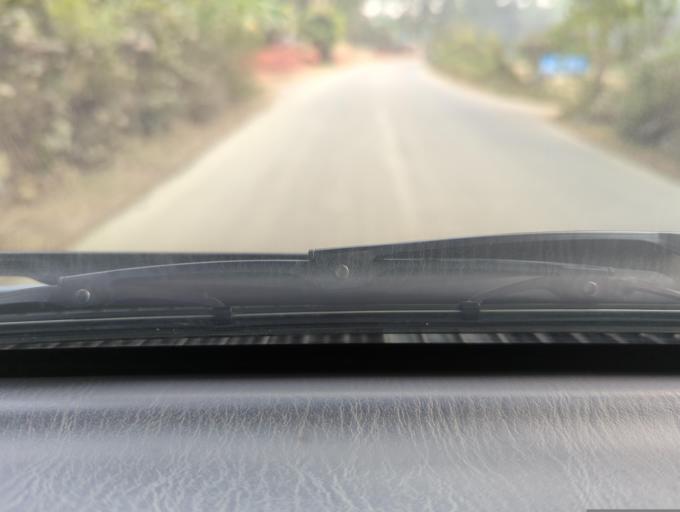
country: BD
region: Sylhet
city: Maulavi Bazar
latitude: 24.5040
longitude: 91.7356
